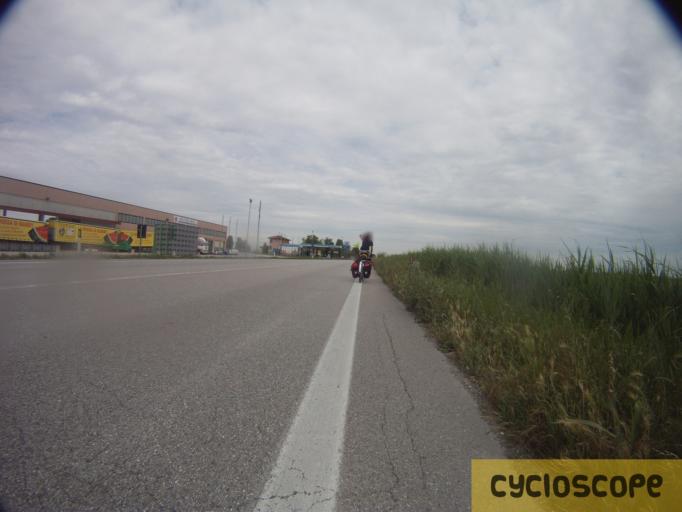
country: IT
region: Emilia-Romagna
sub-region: Provincia di Ferrara
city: Mesola
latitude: 44.9412
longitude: 12.2269
